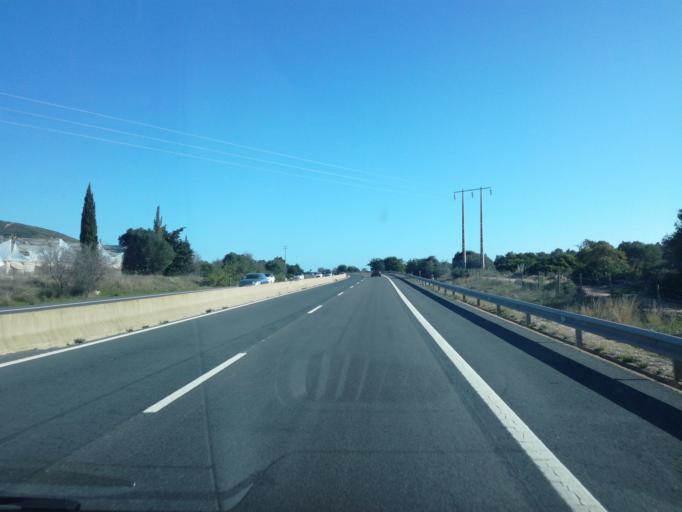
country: PT
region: Faro
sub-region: Faro
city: Santa Barbara de Nexe
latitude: 37.0962
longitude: -7.9530
